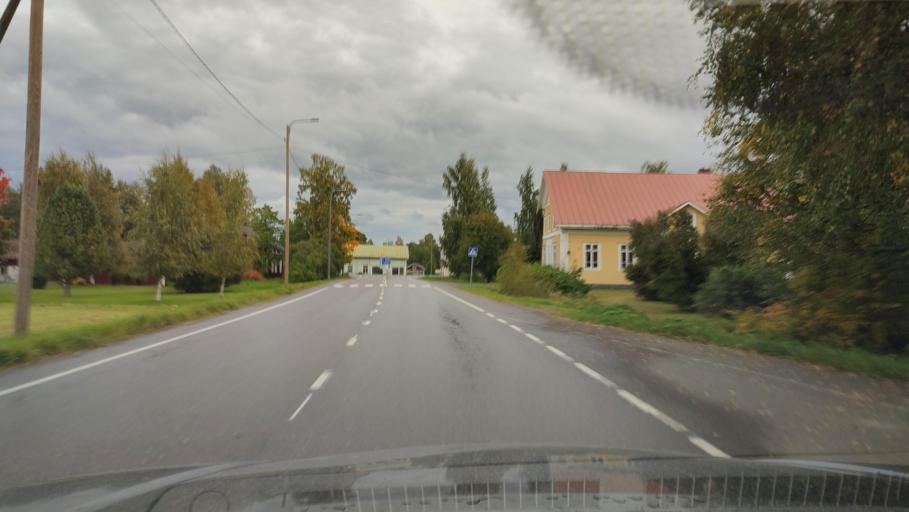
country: FI
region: Ostrobothnia
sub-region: Sydosterbotten
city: Kristinestad
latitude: 62.2574
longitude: 21.5246
